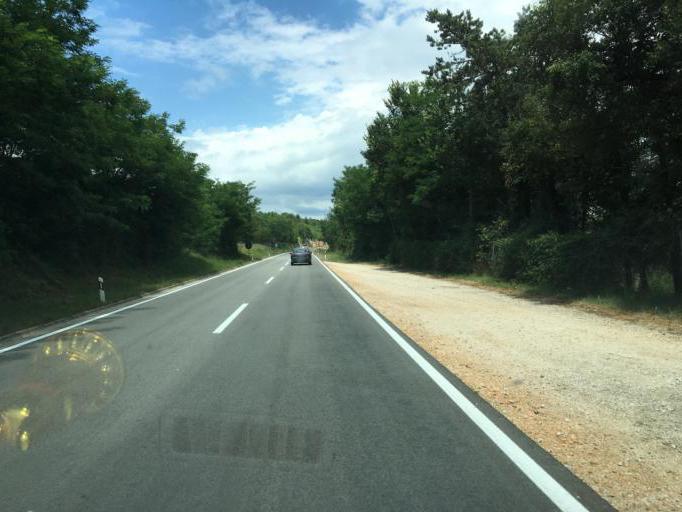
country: HR
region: Istarska
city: Karojba
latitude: 45.2275
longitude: 13.8402
